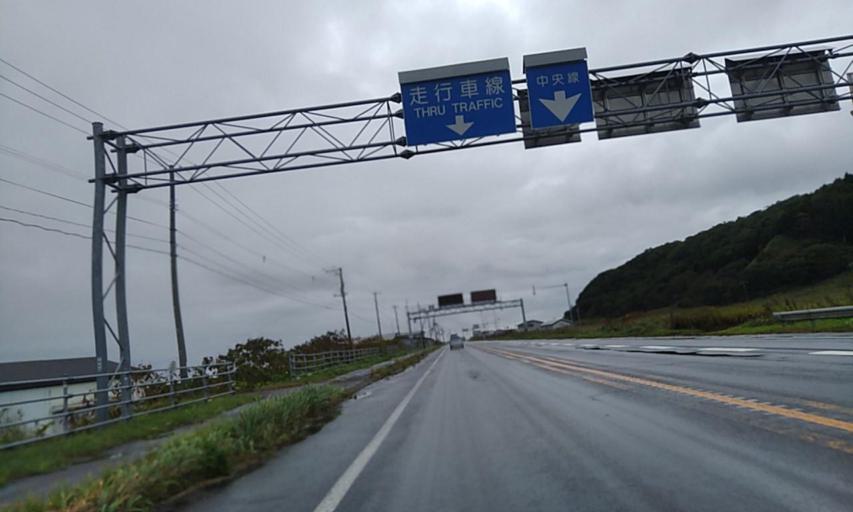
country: JP
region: Hokkaido
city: Kushiro
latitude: 42.9657
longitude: 144.1164
